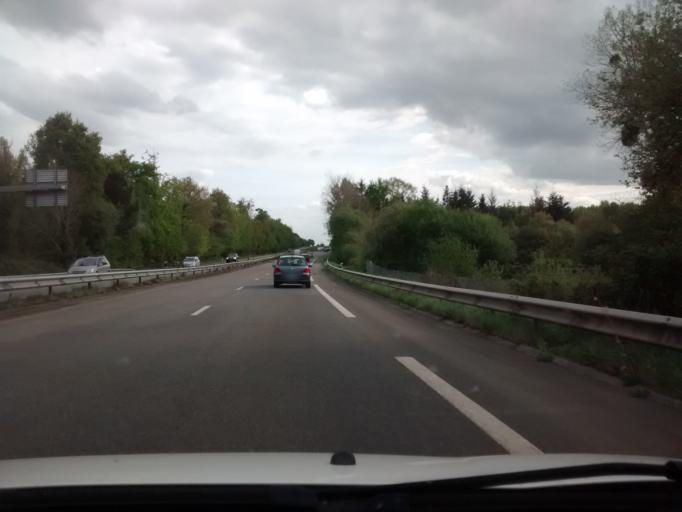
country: FR
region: Brittany
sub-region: Departement d'Ille-et-Vilaine
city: Miniac-Morvan
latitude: 48.4912
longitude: -1.9061
